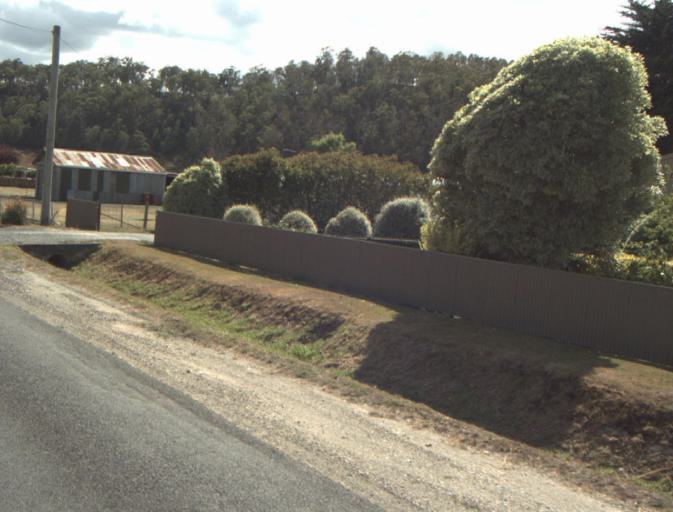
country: AU
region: Tasmania
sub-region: Launceston
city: Mayfield
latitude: -41.2508
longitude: 147.1477
